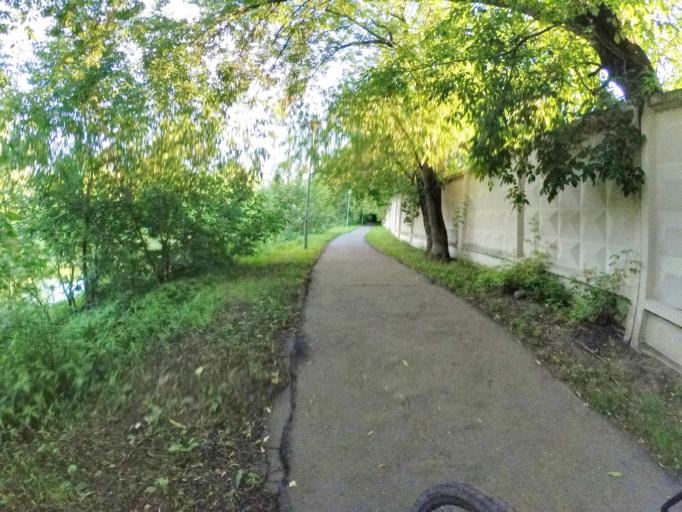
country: RU
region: Moscow
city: Strogino
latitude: 55.8317
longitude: 37.4270
